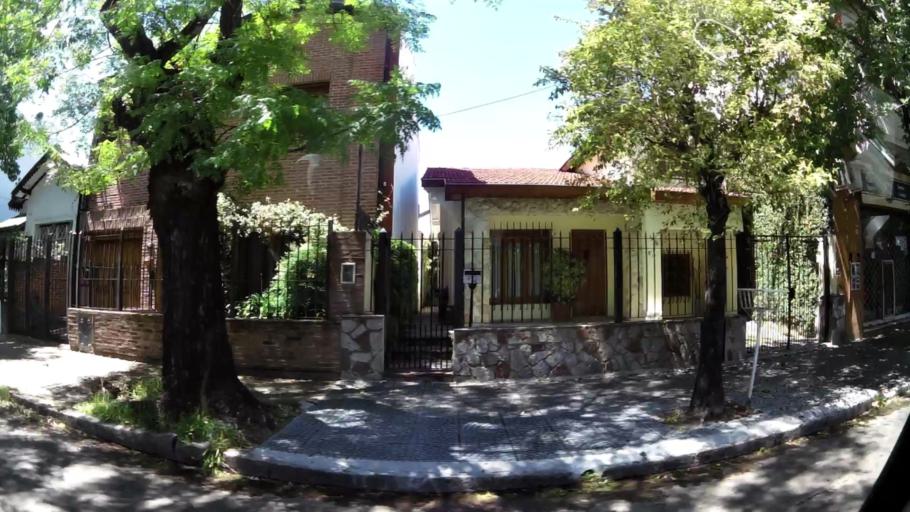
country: AR
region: Buenos Aires
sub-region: Partido de Vicente Lopez
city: Olivos
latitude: -34.5095
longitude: -58.4949
